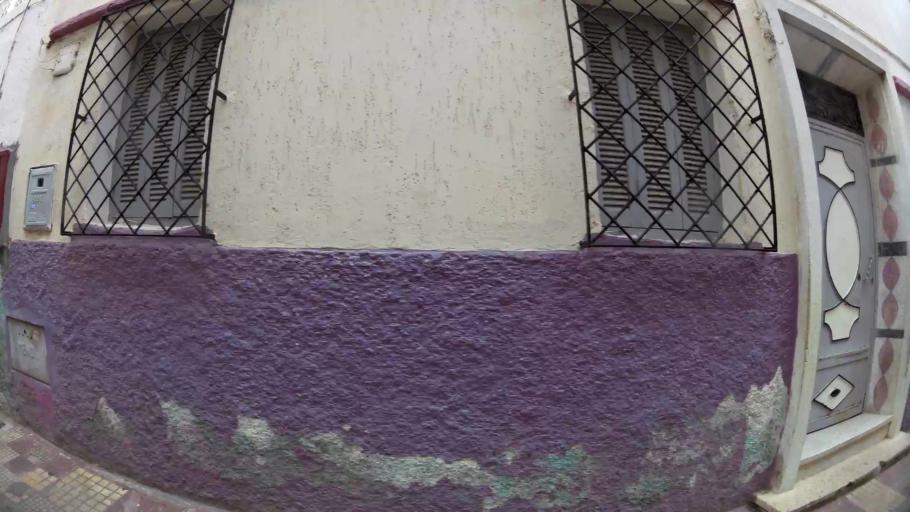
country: MA
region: Tanger-Tetouan
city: Tetouan
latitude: 35.5757
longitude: -5.3525
